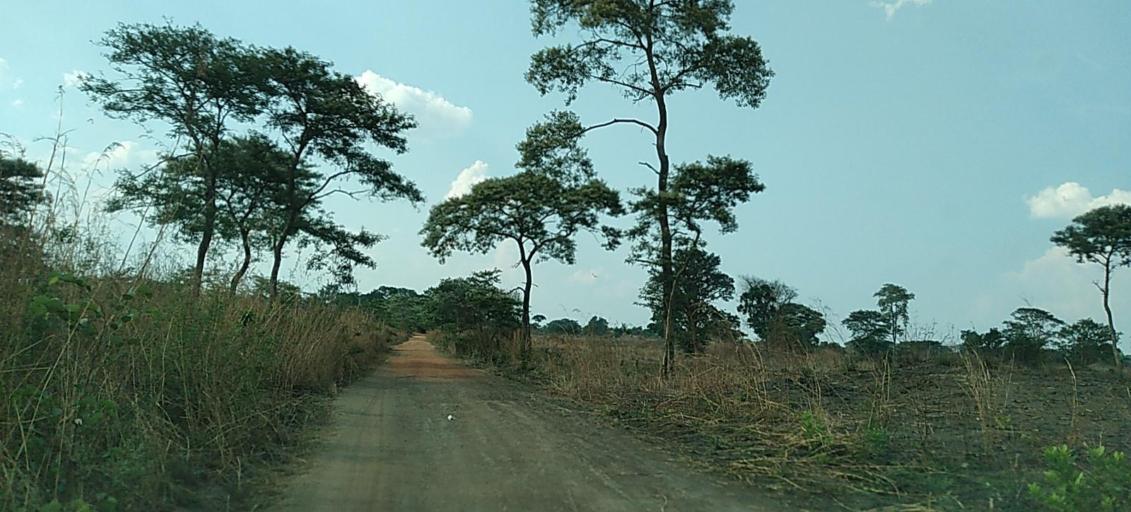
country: ZM
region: Copperbelt
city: Mpongwe
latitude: -13.4985
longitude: 28.0876
